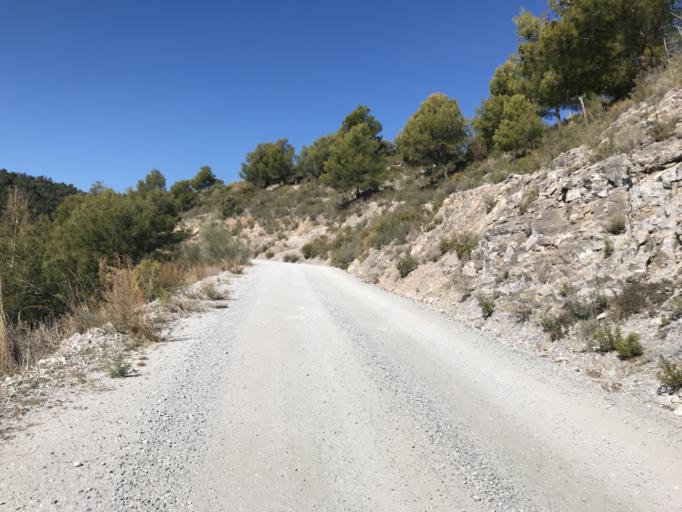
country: ES
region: Andalusia
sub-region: Provincia de Malaga
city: Canillas de Albaida
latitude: 36.8578
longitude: -3.9878
